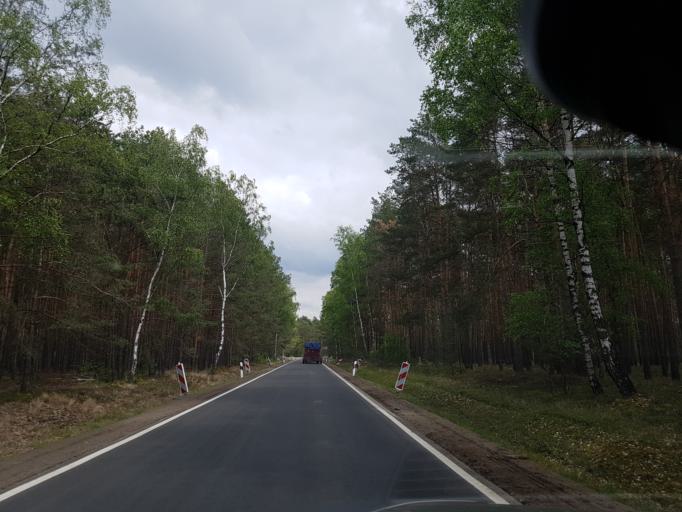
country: DE
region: Brandenburg
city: Finsterwalde
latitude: 51.6558
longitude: 13.7674
